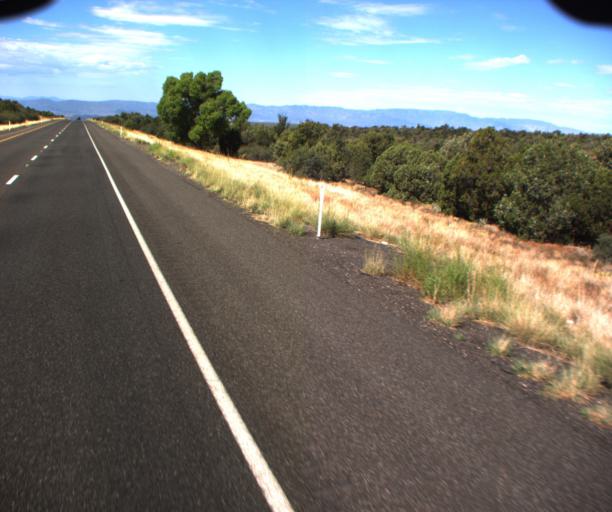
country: US
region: Arizona
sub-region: Yavapai County
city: Village of Oak Creek (Big Park)
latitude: 34.7482
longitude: -111.6802
